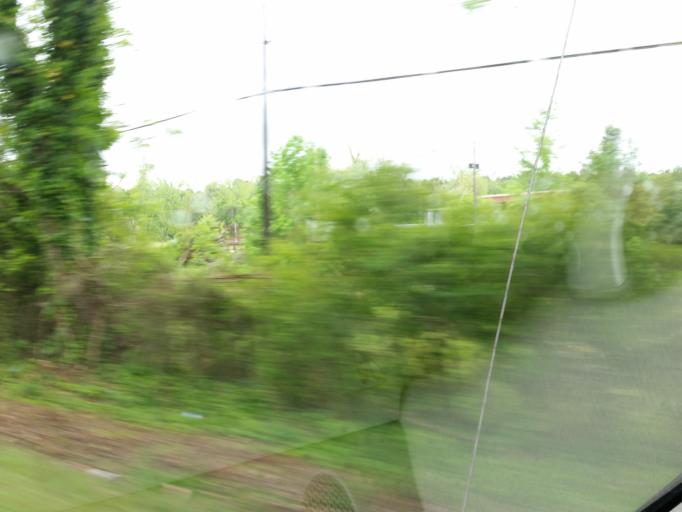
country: US
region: Georgia
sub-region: Lamar County
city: Barnesville
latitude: 33.1069
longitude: -84.1903
